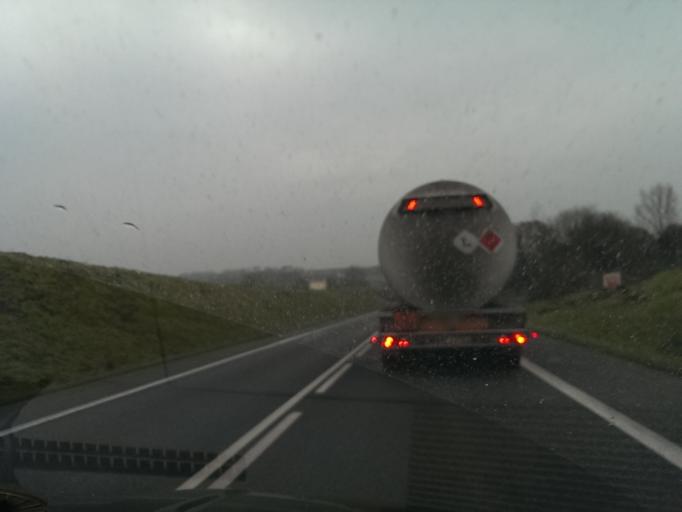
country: PL
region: Kujawsko-Pomorskie
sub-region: Powiat nakielski
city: Slesin
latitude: 53.1678
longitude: 17.6873
